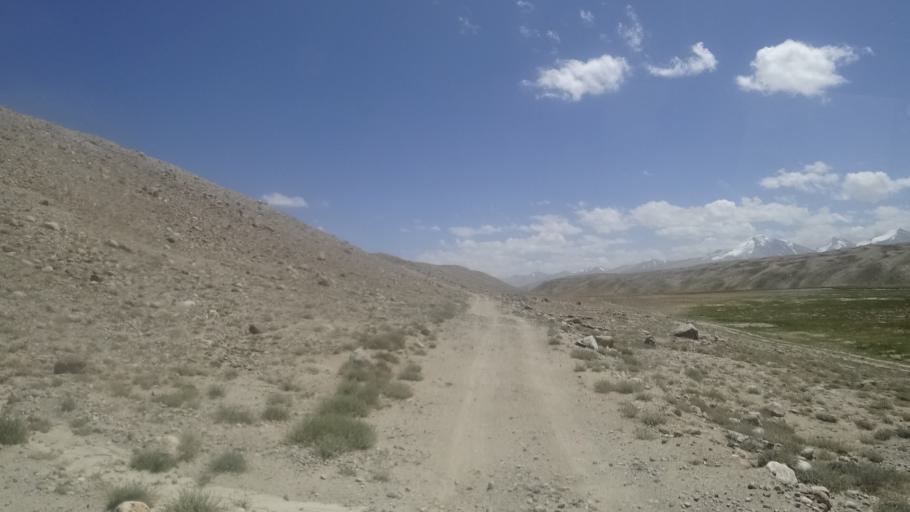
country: TJ
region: Gorno-Badakhshan
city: Murghob
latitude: 37.4648
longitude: 73.3488
